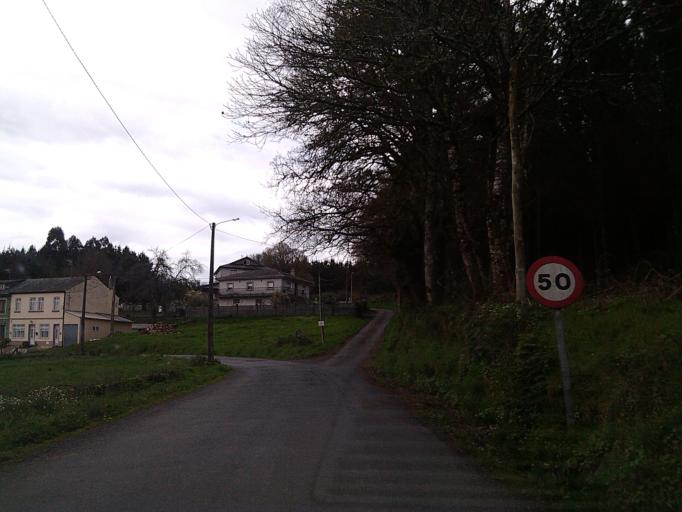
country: ES
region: Galicia
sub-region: Provincia de Lugo
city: Guitiriz
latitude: 43.1596
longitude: -7.8378
